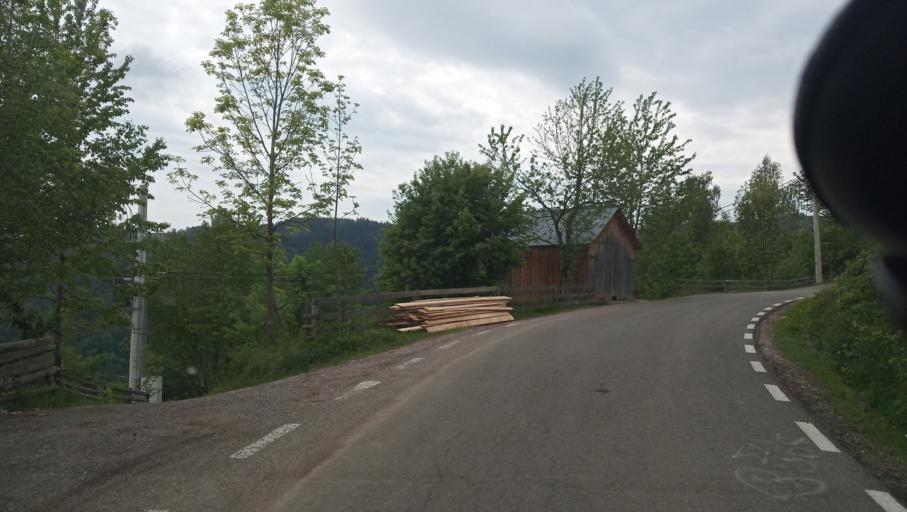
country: RO
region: Alba
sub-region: Comuna Horea
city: Horea
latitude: 46.5075
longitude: 22.9066
